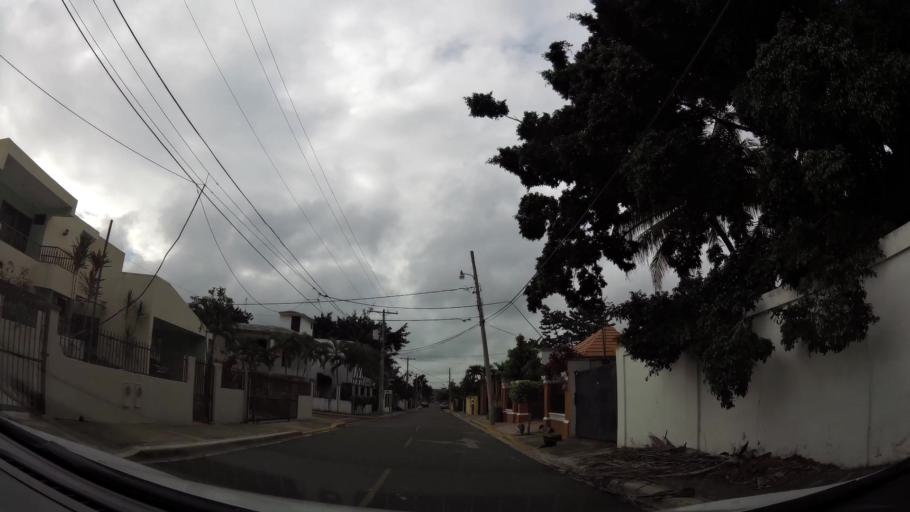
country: DO
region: Santiago
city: Santiago de los Caballeros
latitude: 19.4663
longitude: -70.6553
